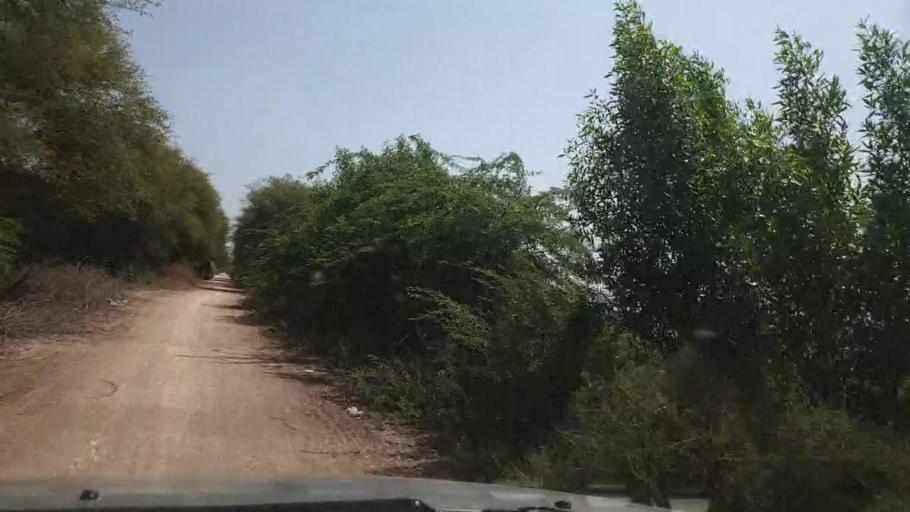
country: PK
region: Sindh
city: Tando Ghulam Ali
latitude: 25.1025
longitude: 68.7858
